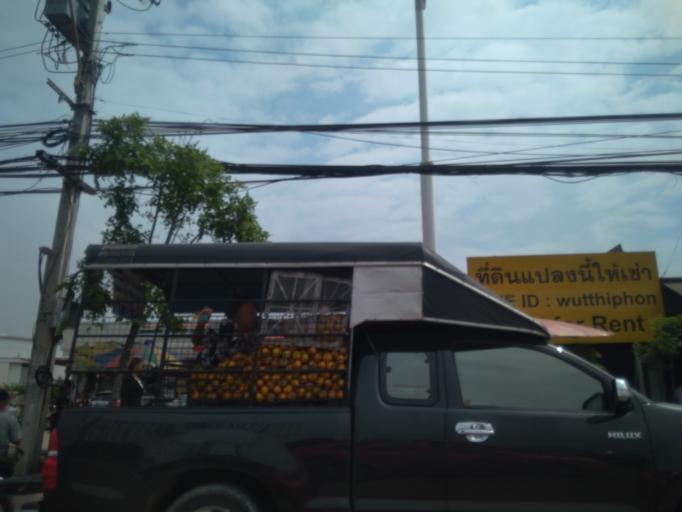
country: TH
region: Bangkok
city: Suan Luang
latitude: 13.7297
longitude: 100.6416
